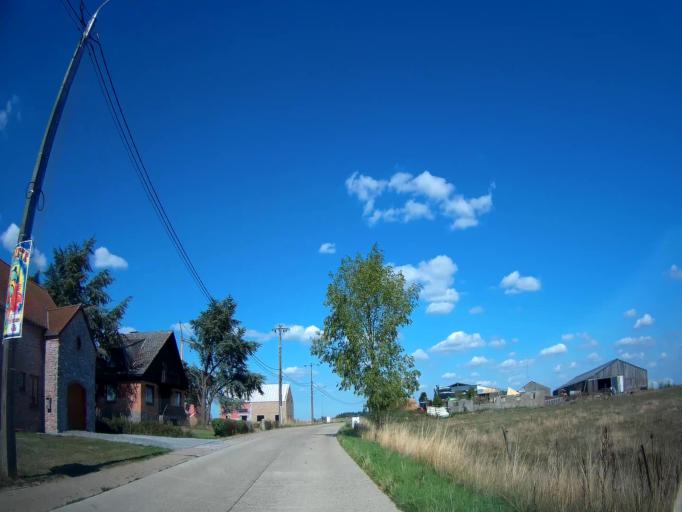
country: FR
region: Champagne-Ardenne
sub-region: Departement des Ardennes
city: Fromelennes
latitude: 50.1671
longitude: 4.8924
